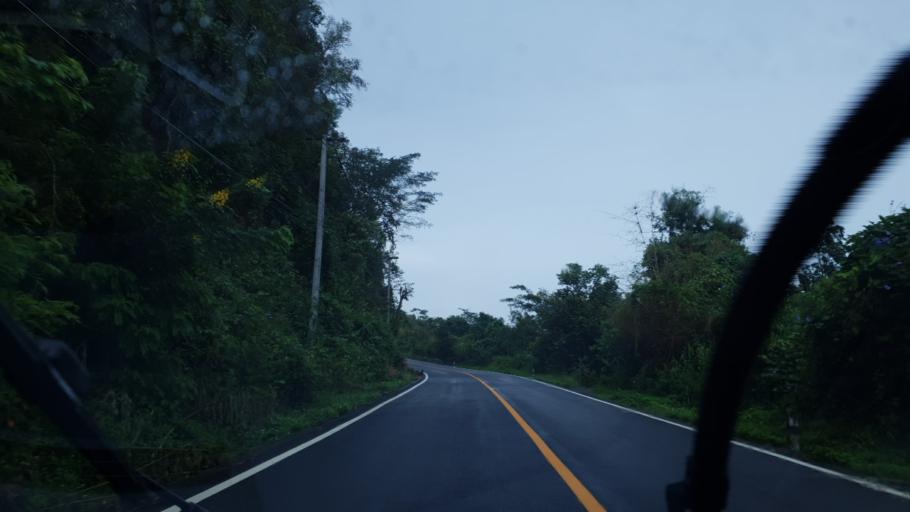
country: TH
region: Mae Hong Son
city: Ban Huai I Huak
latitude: 18.1427
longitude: 98.1042
